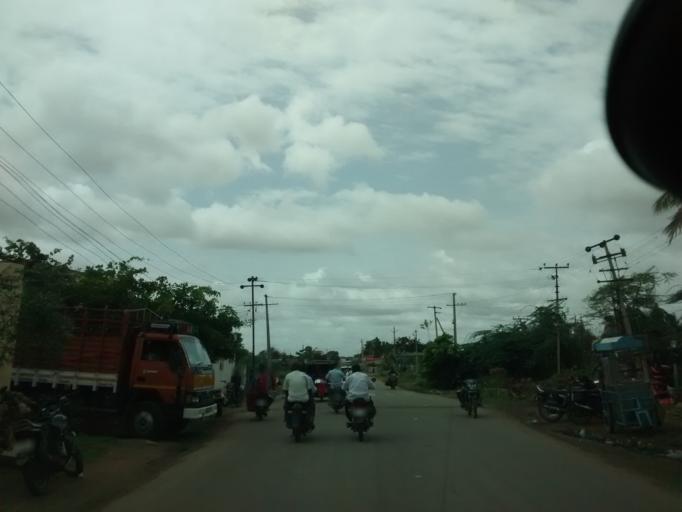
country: IN
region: Andhra Pradesh
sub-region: Anantapur
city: Hindupur
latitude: 13.8453
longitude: 77.4831
